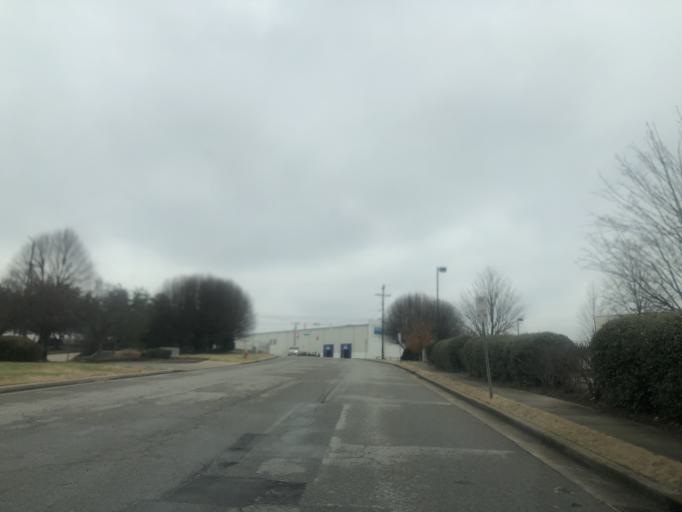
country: US
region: Tennessee
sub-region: Davidson County
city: Lakewood
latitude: 36.1462
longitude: -86.6731
